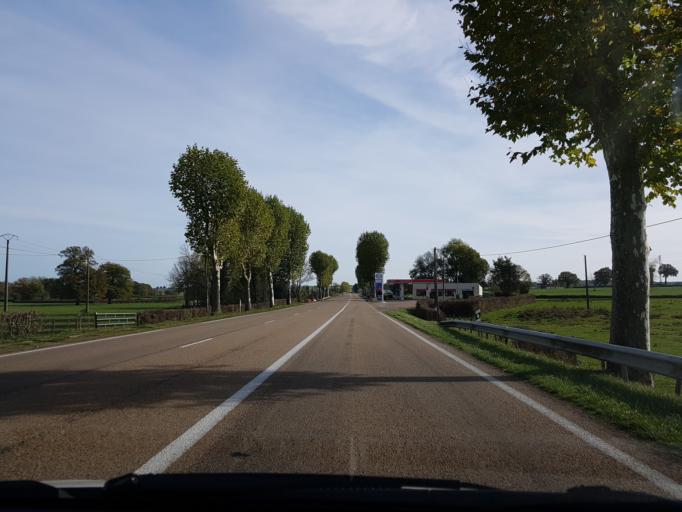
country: FR
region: Bourgogne
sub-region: Departement de l'Yonne
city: Avallon
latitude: 47.4776
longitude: 4.0107
